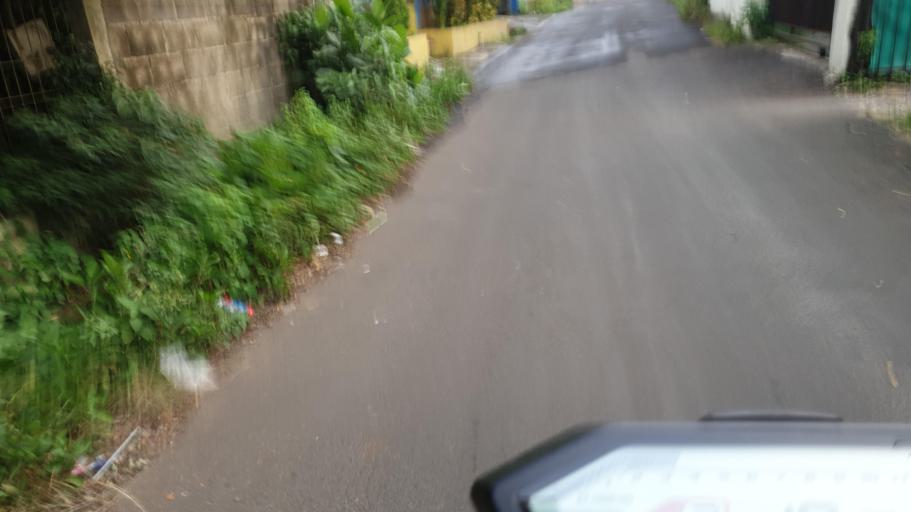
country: ID
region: West Java
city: Depok
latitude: -6.3657
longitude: 106.8377
